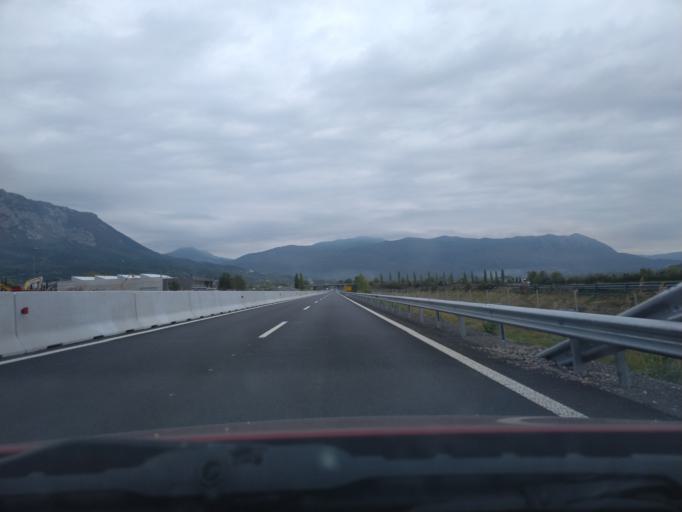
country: SI
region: Ajdovscina
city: Ajdovscina
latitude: 45.8816
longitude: 13.8960
